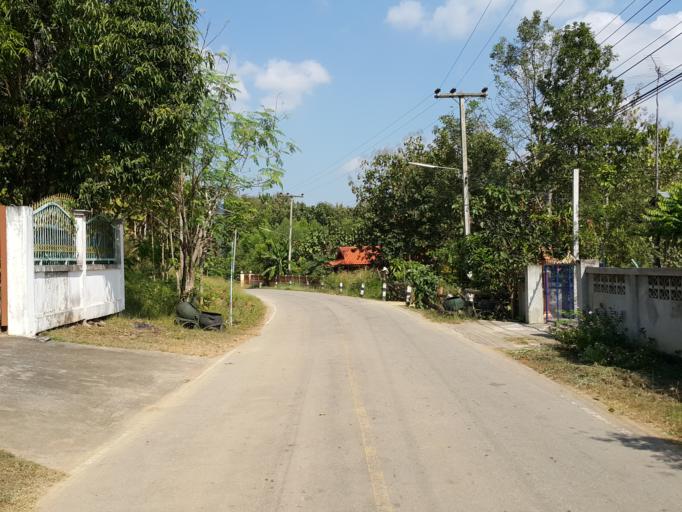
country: TH
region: Sukhothai
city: Thung Saliam
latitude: 17.3349
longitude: 99.4580
